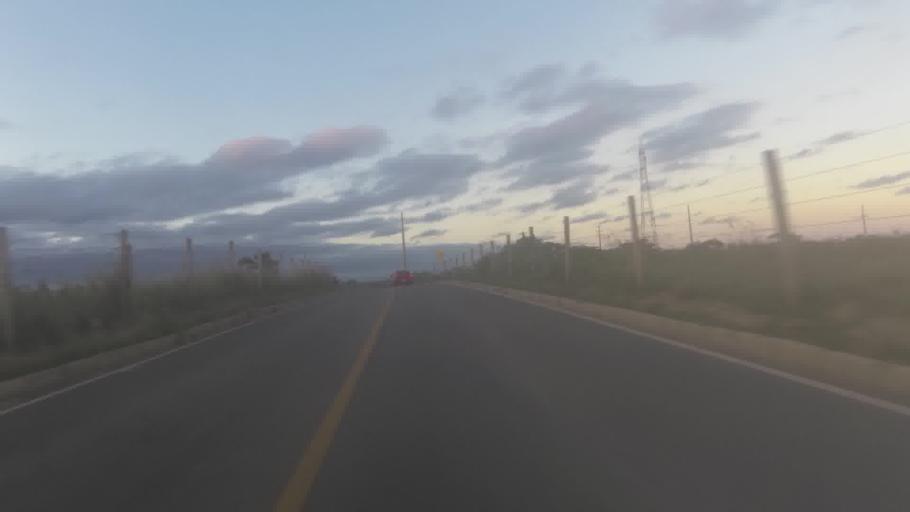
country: BR
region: Espirito Santo
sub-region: Marataizes
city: Marataizes
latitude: -21.0361
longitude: -40.8418
